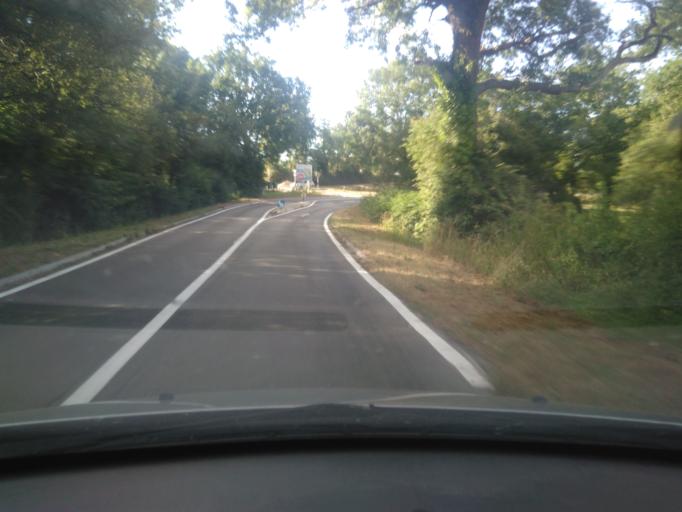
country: FR
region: Pays de la Loire
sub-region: Departement de la Vendee
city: Saint-Florent-des-Bois
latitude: 46.5856
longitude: -1.3179
